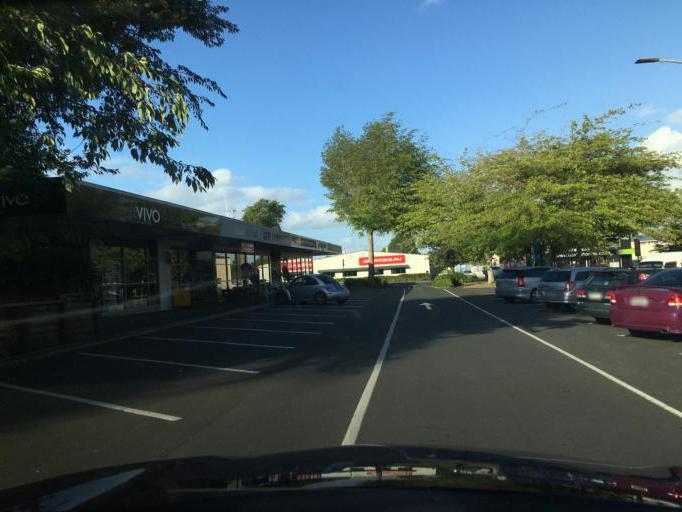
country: NZ
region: Waikato
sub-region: Waipa District
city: Cambridge
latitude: -38.0108
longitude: 175.3274
